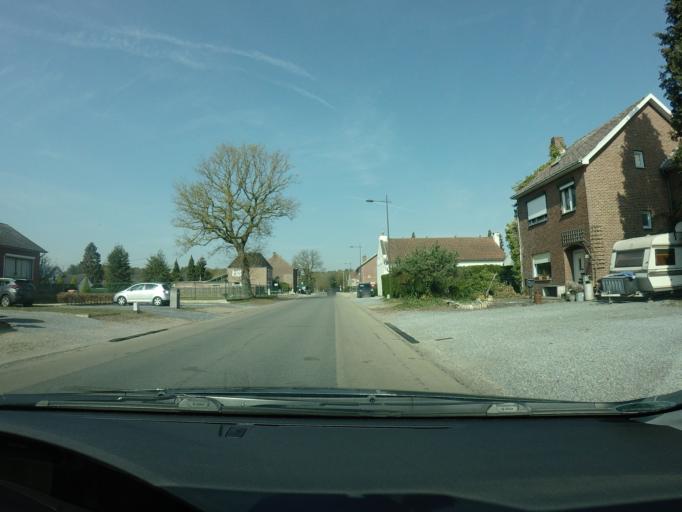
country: BE
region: Flanders
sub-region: Provincie Limburg
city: Maasmechelen
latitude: 50.9497
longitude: 5.6699
